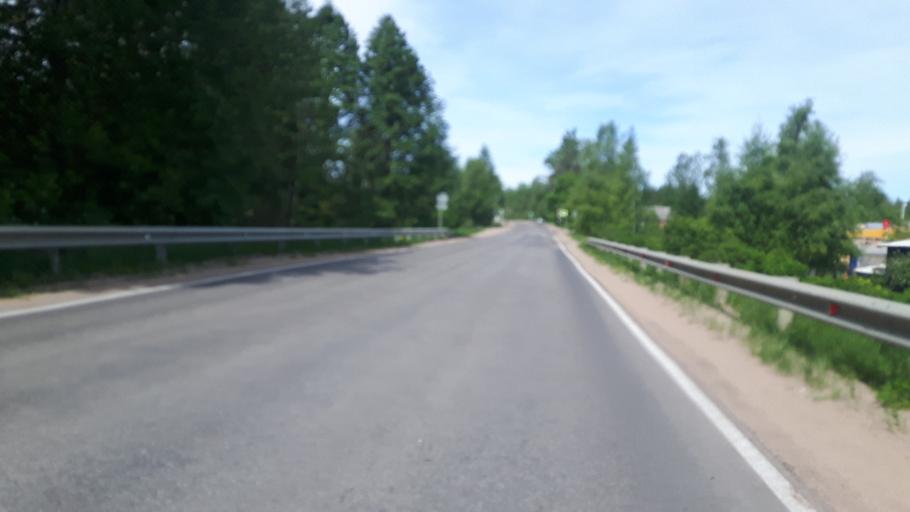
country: RU
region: Leningrad
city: Ust'-Luga
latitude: 59.6549
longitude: 28.2557
